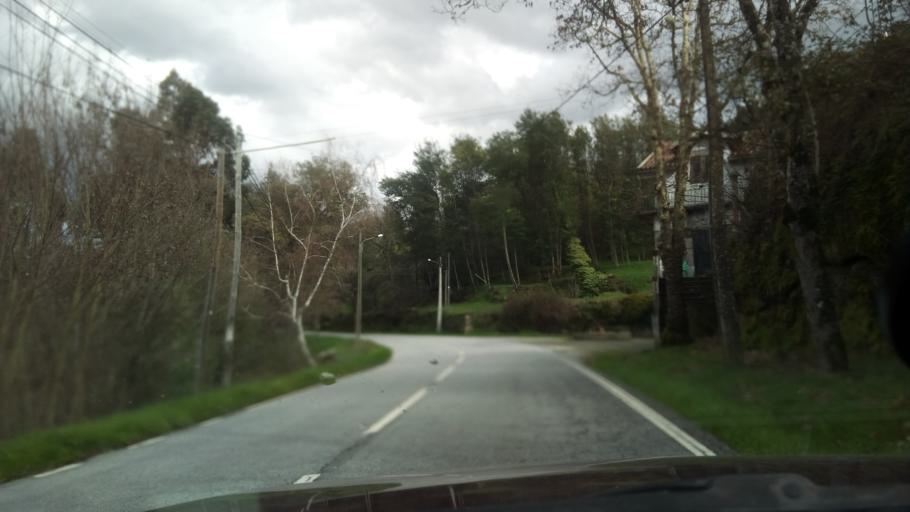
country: PT
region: Guarda
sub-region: Fornos de Algodres
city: Fornos de Algodres
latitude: 40.6153
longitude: -7.5115
